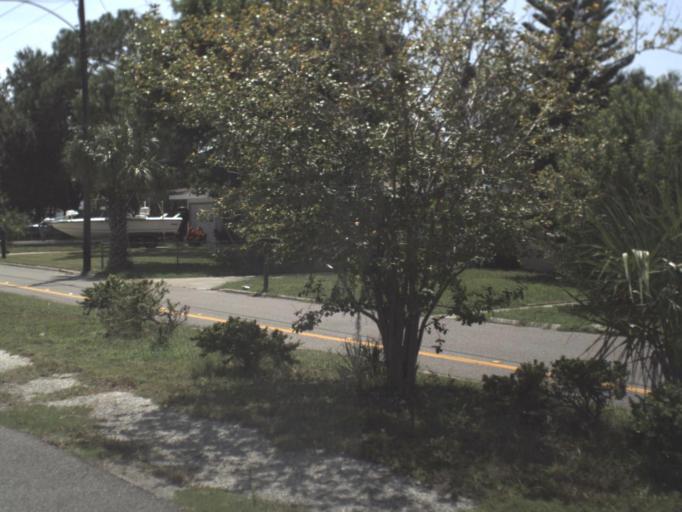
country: US
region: Florida
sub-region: Pinellas County
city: Dunedin
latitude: 28.0468
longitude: -82.7814
